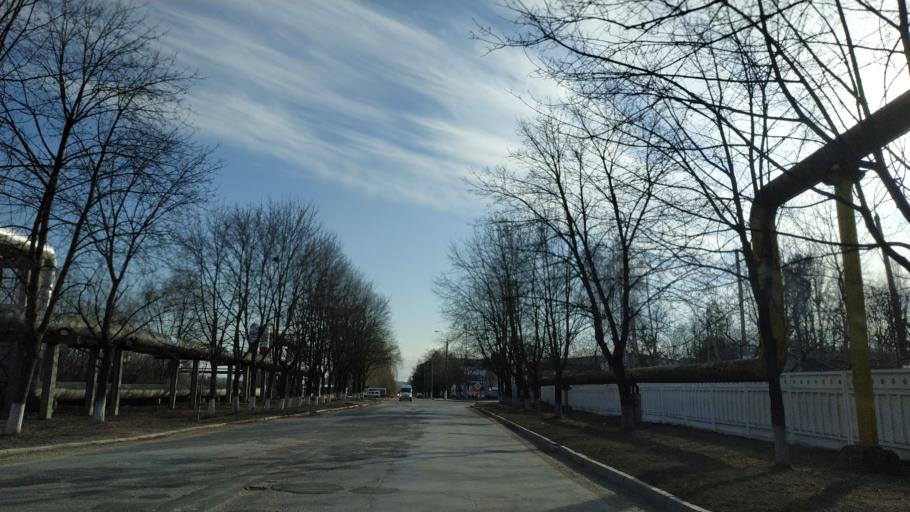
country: MD
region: Chisinau
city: Chisinau
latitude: 47.0277
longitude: 28.8959
